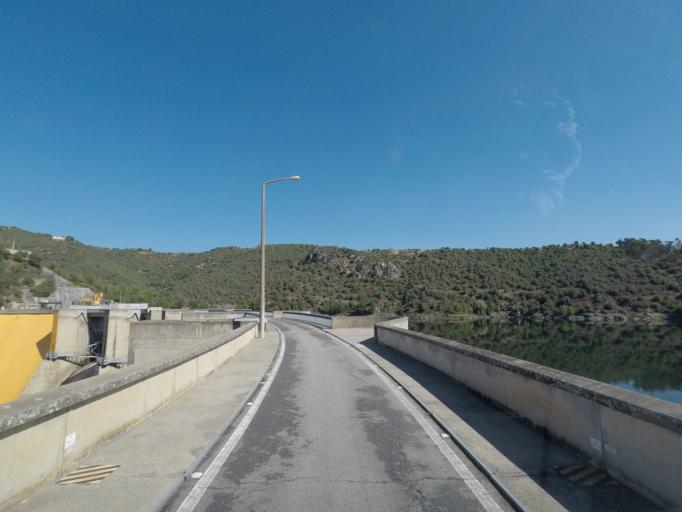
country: ES
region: Castille and Leon
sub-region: Provincia de Salamanca
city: Villarino de los Aires
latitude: 41.3000
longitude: -6.4694
